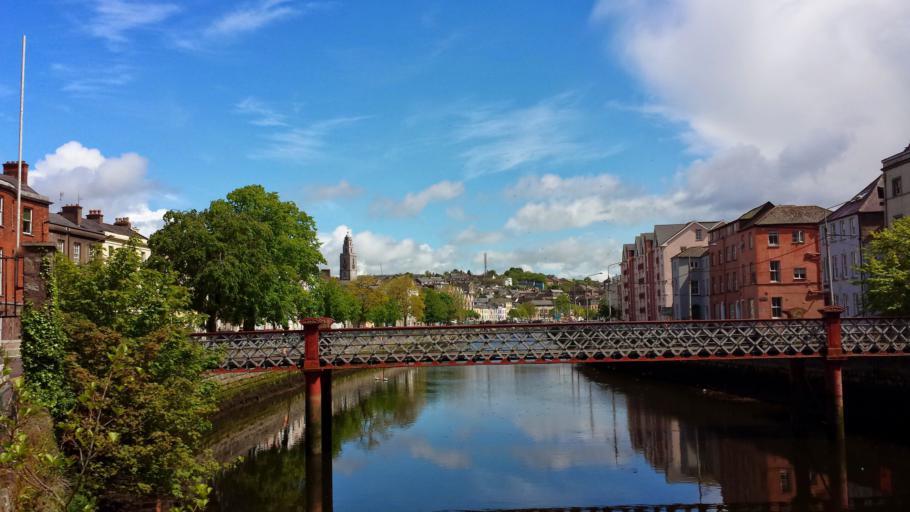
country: IE
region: Munster
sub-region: County Cork
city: Cork
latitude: 51.9001
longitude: -8.4839
